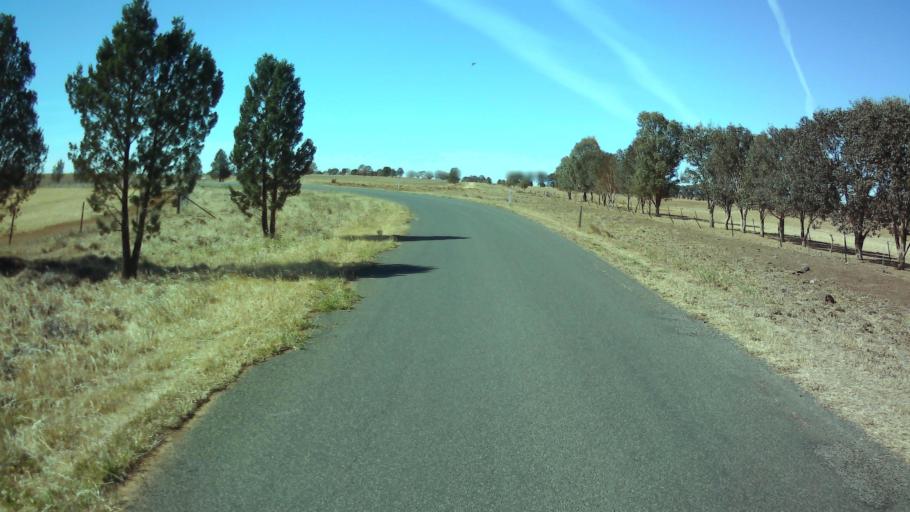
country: AU
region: New South Wales
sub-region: Weddin
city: Grenfell
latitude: -34.0474
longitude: 148.1735
